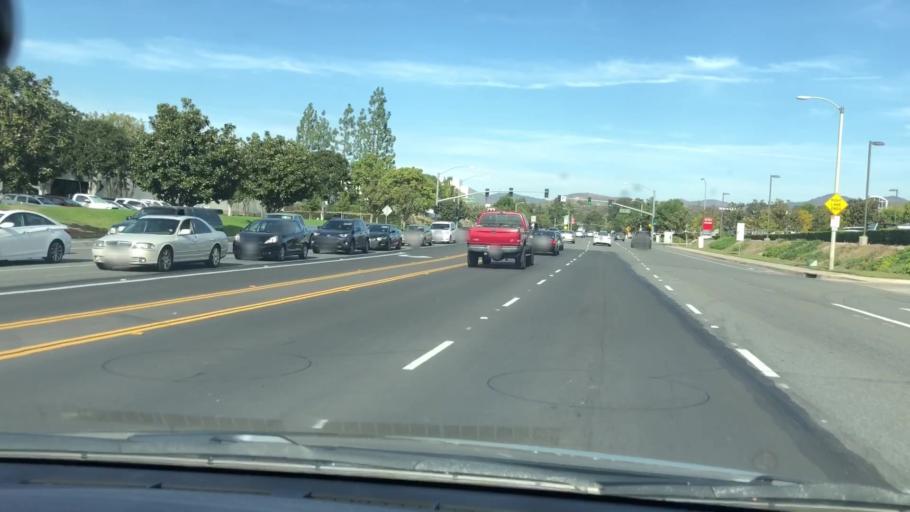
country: US
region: California
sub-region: Orange County
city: Lake Forest
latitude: 33.6559
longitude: -117.7022
